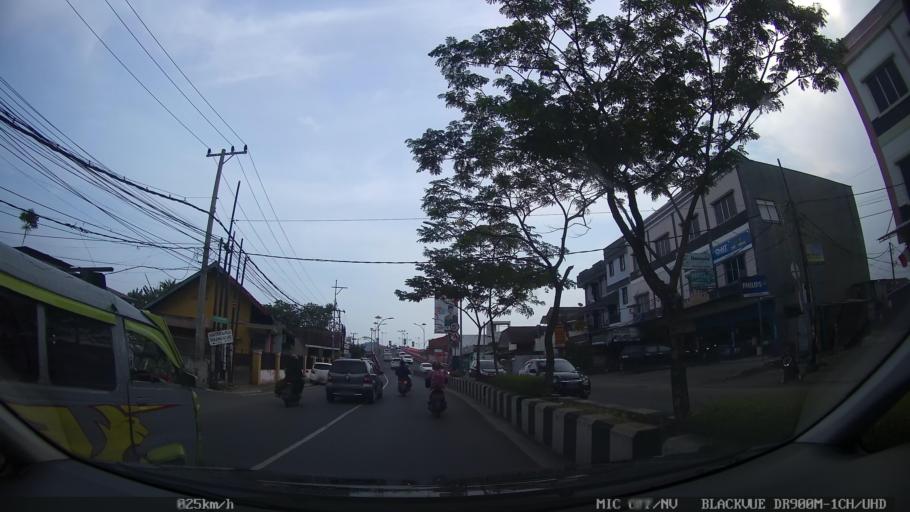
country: ID
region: Lampung
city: Bandarlampung
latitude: -5.4117
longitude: 105.2678
